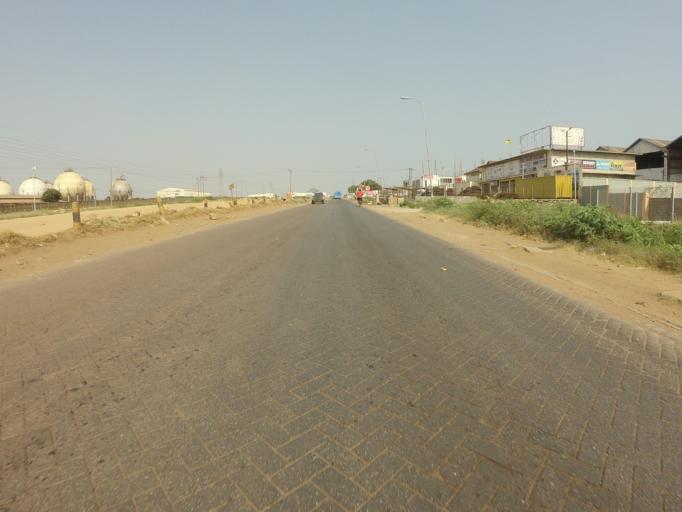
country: GH
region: Greater Accra
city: Tema
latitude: 5.6655
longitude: 0.0067
